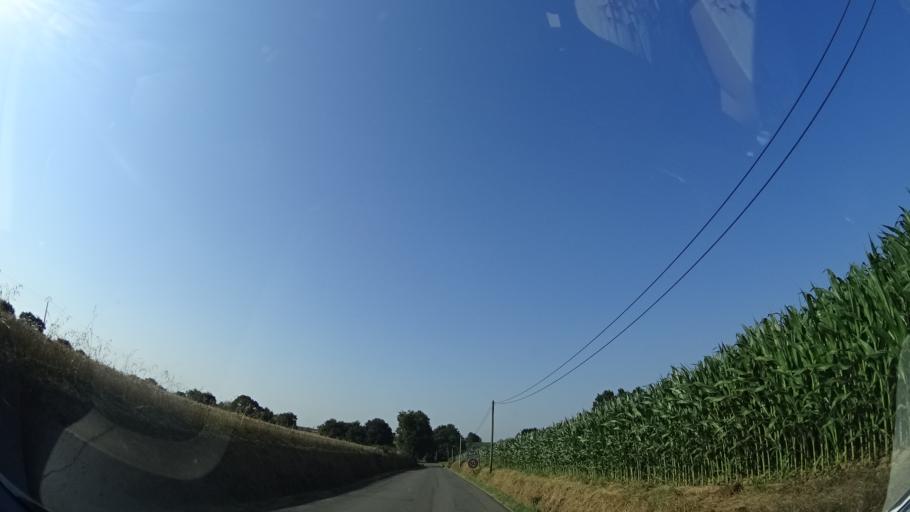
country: FR
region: Brittany
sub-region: Departement d'Ille-et-Vilaine
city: Geveze
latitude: 48.1815
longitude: -1.7943
